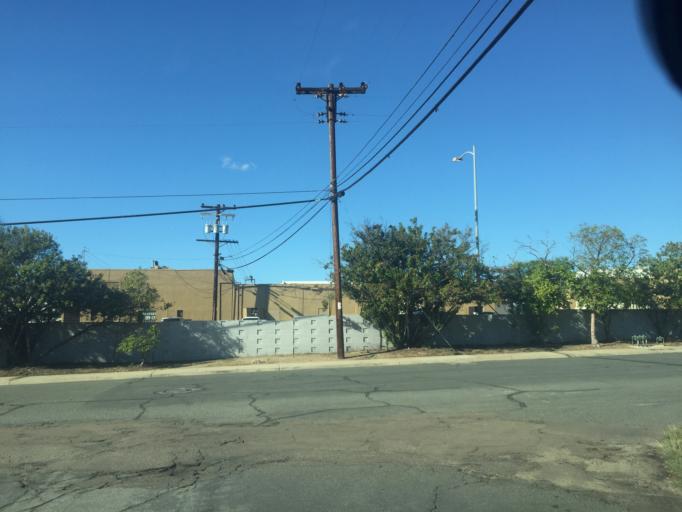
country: US
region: California
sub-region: San Diego County
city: La Mesa
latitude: 32.7904
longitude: -117.0805
